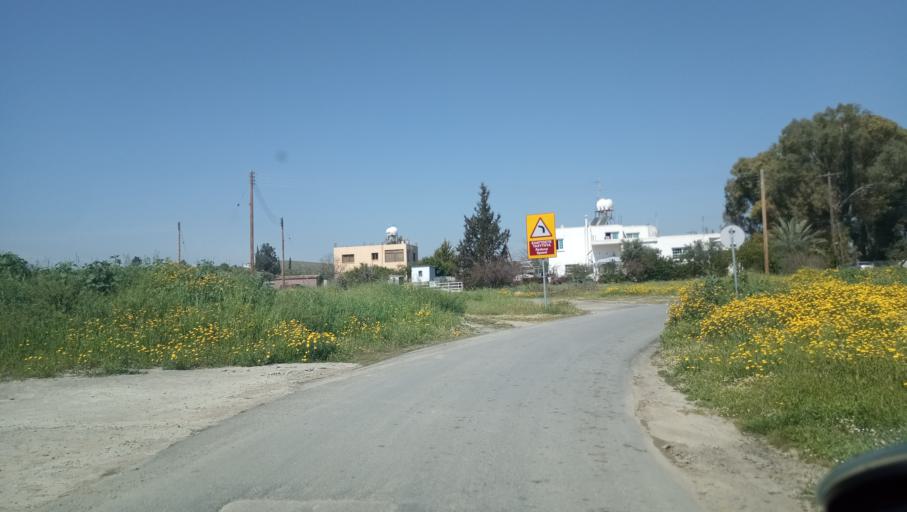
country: CY
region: Lefkosia
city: Alampra
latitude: 35.0148
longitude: 33.3872
